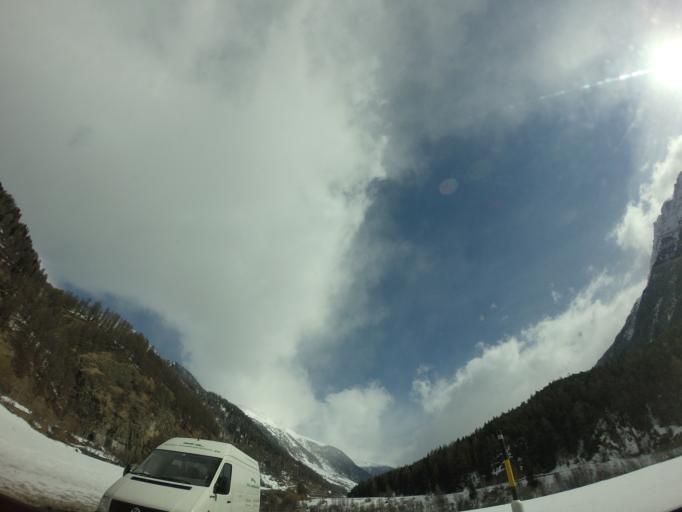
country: CH
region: Grisons
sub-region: Inn District
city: Zernez
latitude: 46.7570
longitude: 10.0873
